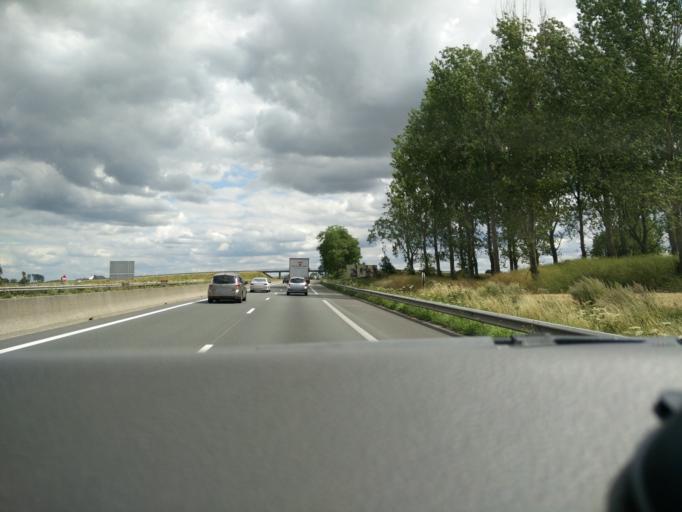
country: FR
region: Nord-Pas-de-Calais
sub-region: Departement du Nord
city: Quaedypre
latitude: 50.9388
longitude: 2.4608
